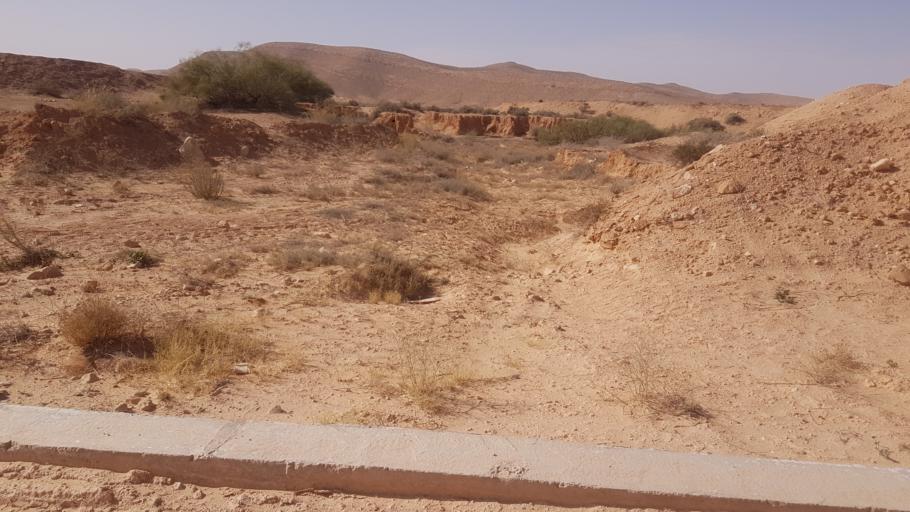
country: TN
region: Qabis
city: El Hamma
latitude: 33.6546
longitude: 9.7357
